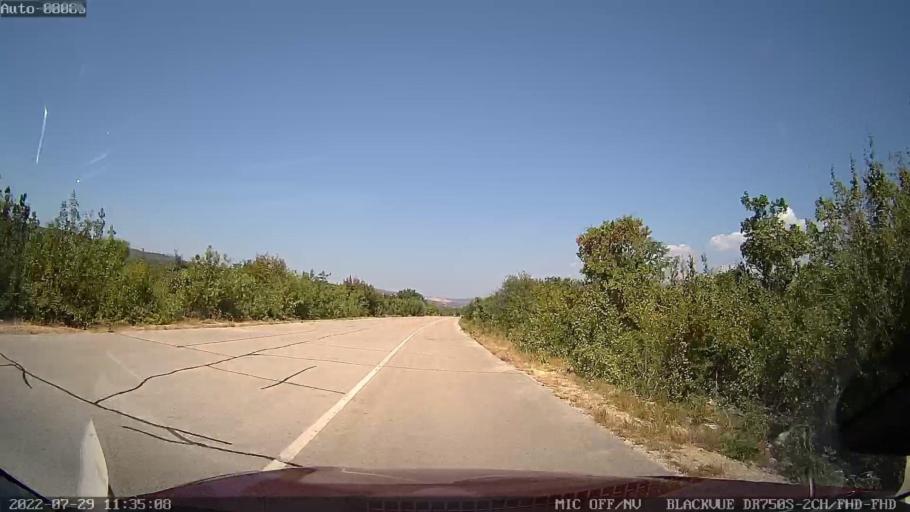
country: HR
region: Zadarska
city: Obrovac
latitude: 44.1807
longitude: 15.7175
